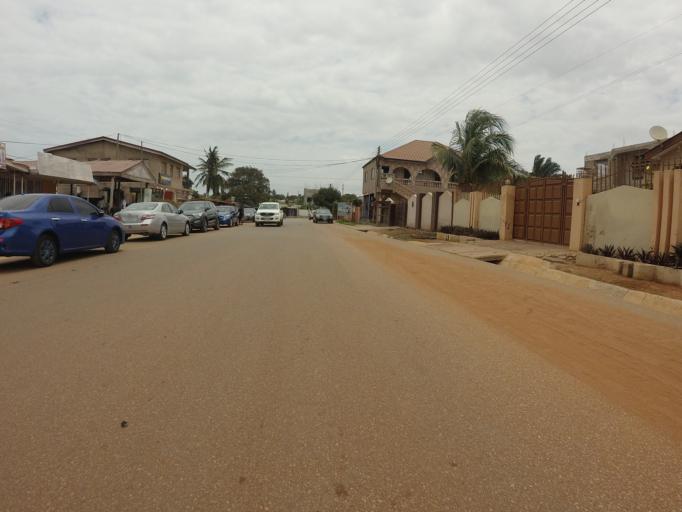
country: GH
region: Greater Accra
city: Teshi Old Town
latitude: 5.6052
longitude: -0.1044
